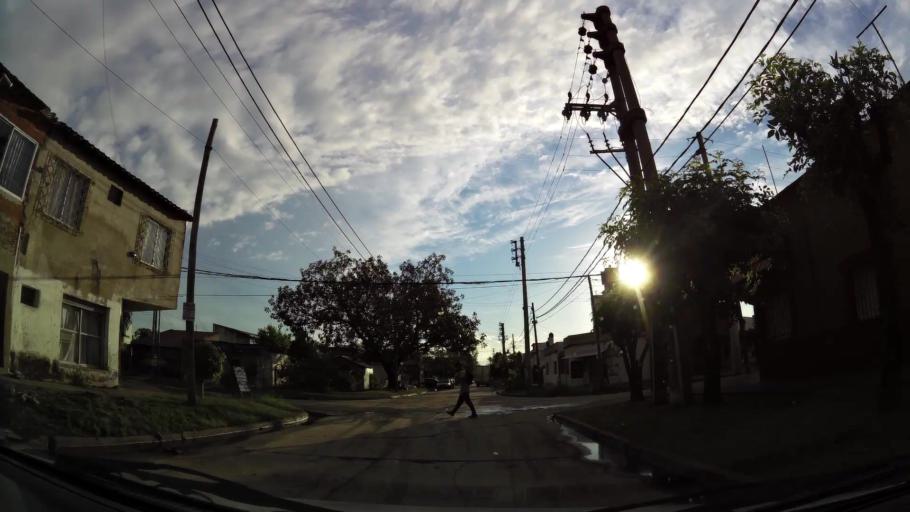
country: AR
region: Buenos Aires
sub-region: Partido de Lomas de Zamora
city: Lomas de Zamora
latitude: -34.7561
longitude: -58.3545
